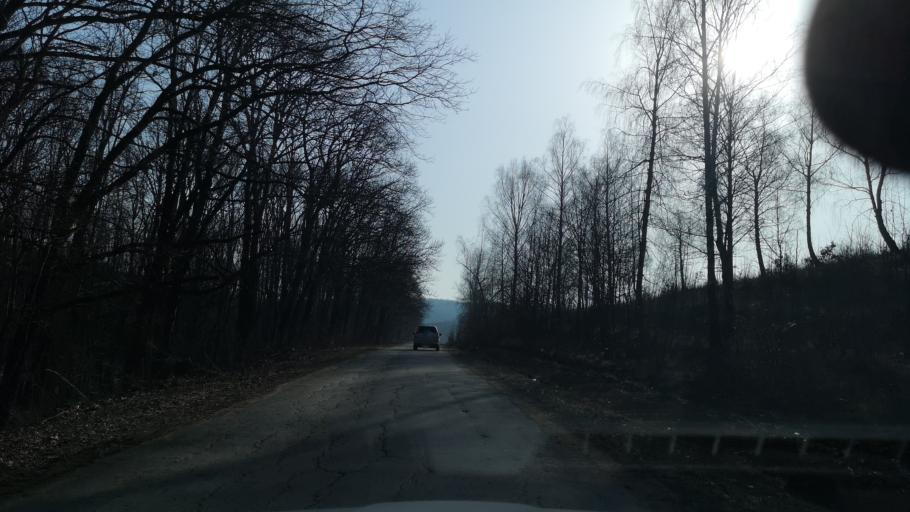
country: MD
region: Nisporeni
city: Nisporeni
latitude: 47.0934
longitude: 28.3156
